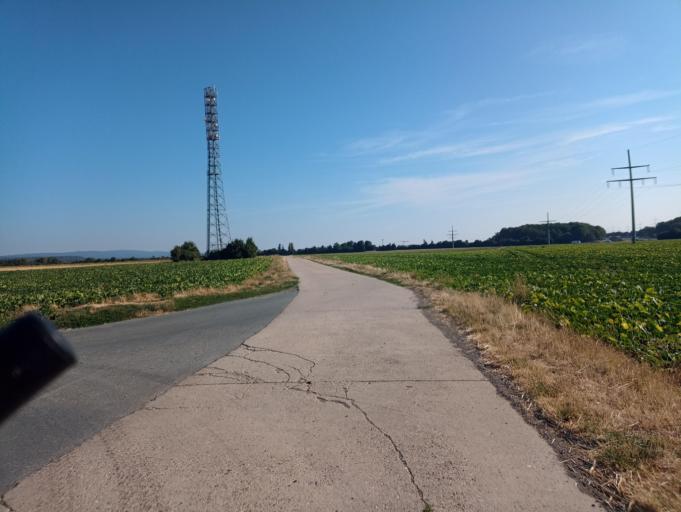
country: DE
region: Hesse
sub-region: Regierungsbezirk Darmstadt
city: Bad Homburg vor der Hoehe
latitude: 50.1965
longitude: 8.6347
